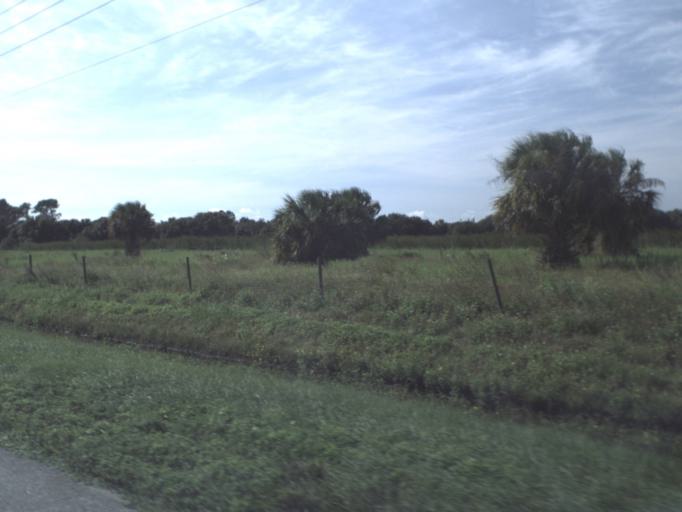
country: US
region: Florida
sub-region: DeSoto County
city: Nocatee
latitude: 27.0583
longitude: -81.7881
